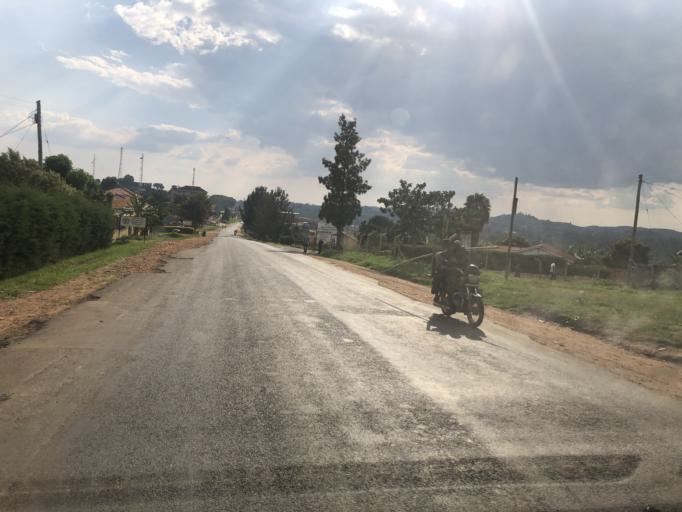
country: UG
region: Western Region
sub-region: Bushenyi District
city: Bushenyi
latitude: -0.5415
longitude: 30.1947
